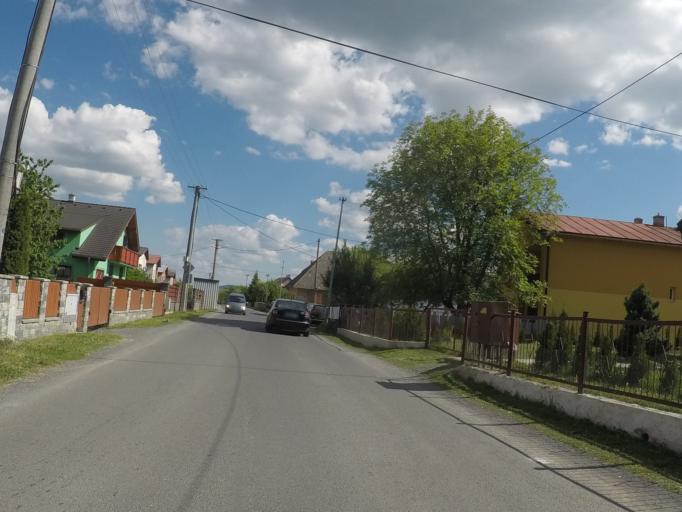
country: SK
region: Presovsky
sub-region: Okres Poprad
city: Poprad
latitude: 49.0182
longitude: 20.3705
